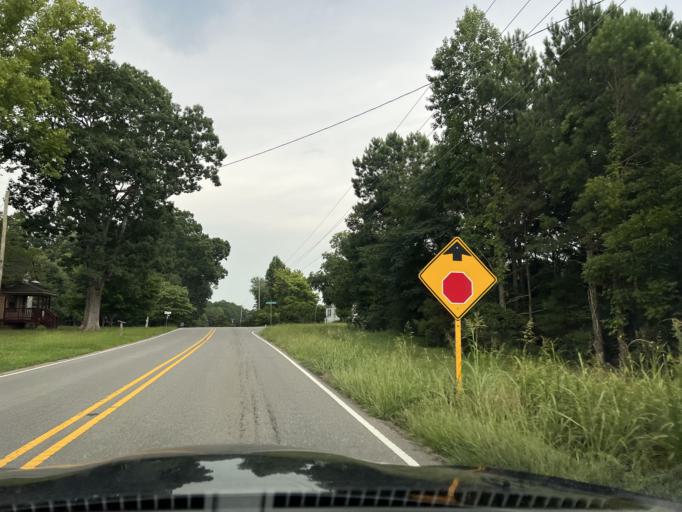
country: US
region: North Carolina
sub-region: Wake County
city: Wake Forest
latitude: 36.0119
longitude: -78.5558
